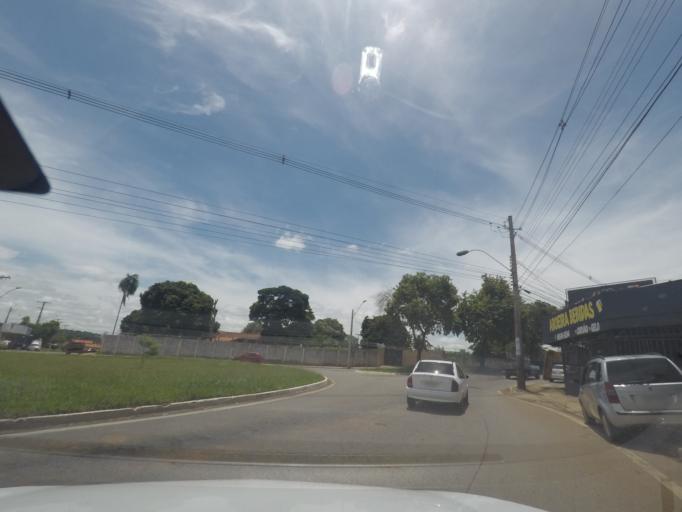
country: BR
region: Goias
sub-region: Goiania
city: Goiania
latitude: -16.6583
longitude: -49.1982
